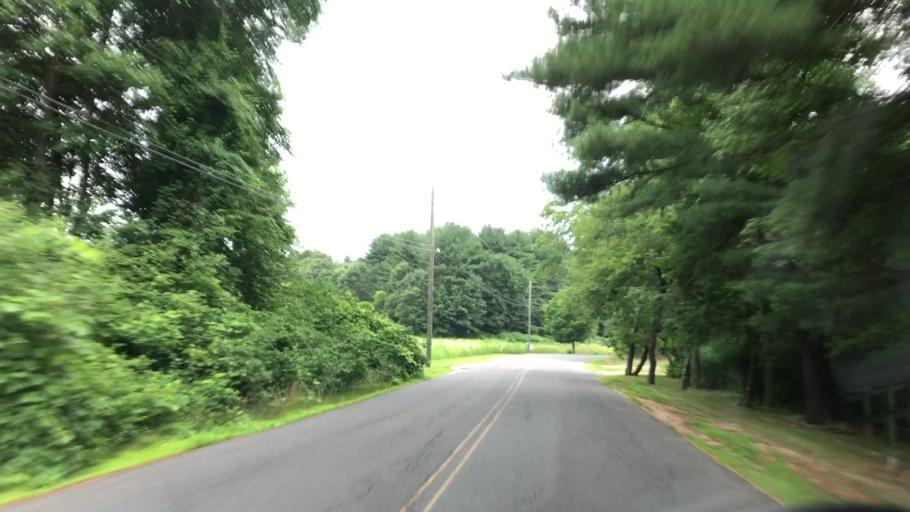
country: US
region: Massachusetts
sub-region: Hampshire County
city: Southampton
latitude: 42.2200
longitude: -72.6842
